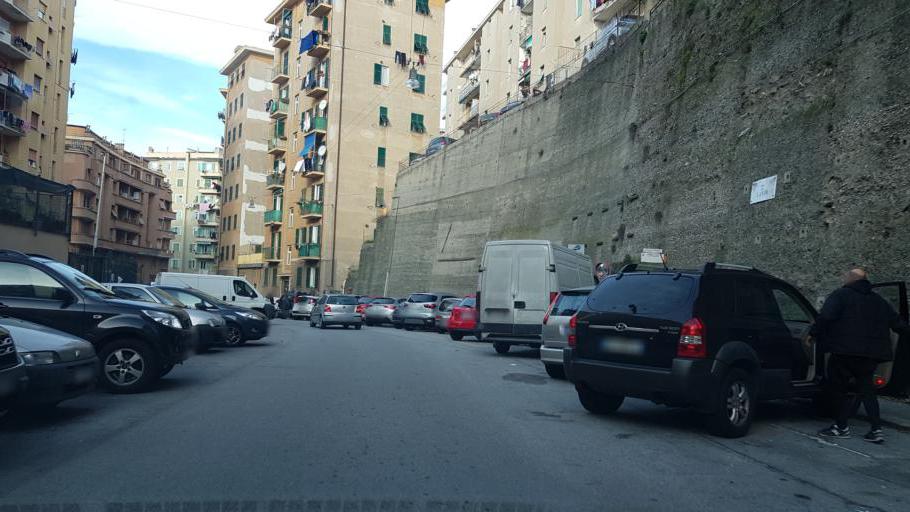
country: IT
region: Liguria
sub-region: Provincia di Genova
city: San Teodoro
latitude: 44.4159
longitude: 8.8920
